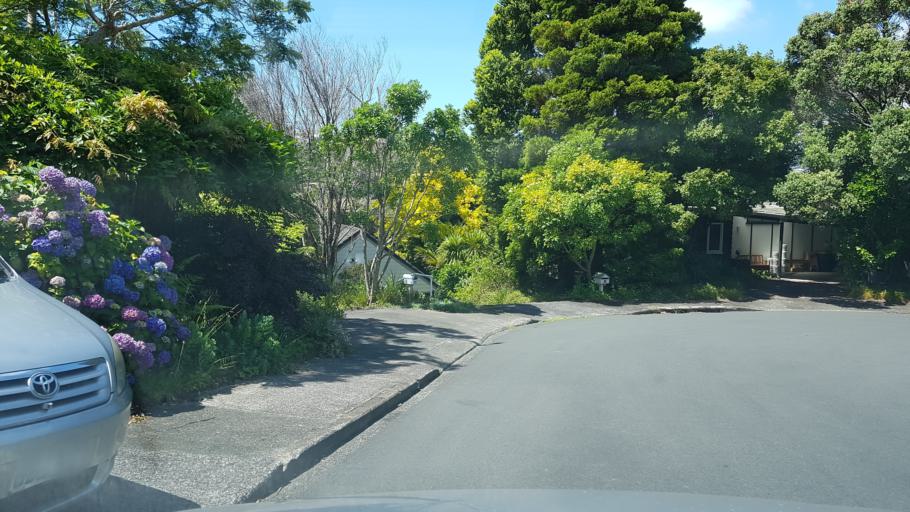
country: NZ
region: Auckland
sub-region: Auckland
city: North Shore
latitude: -36.8152
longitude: 174.7349
